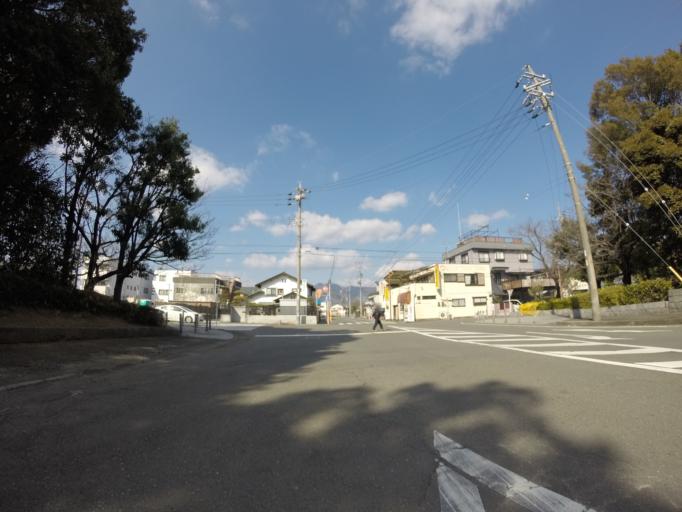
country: JP
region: Shizuoka
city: Shizuoka-shi
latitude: 35.0403
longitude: 138.5021
